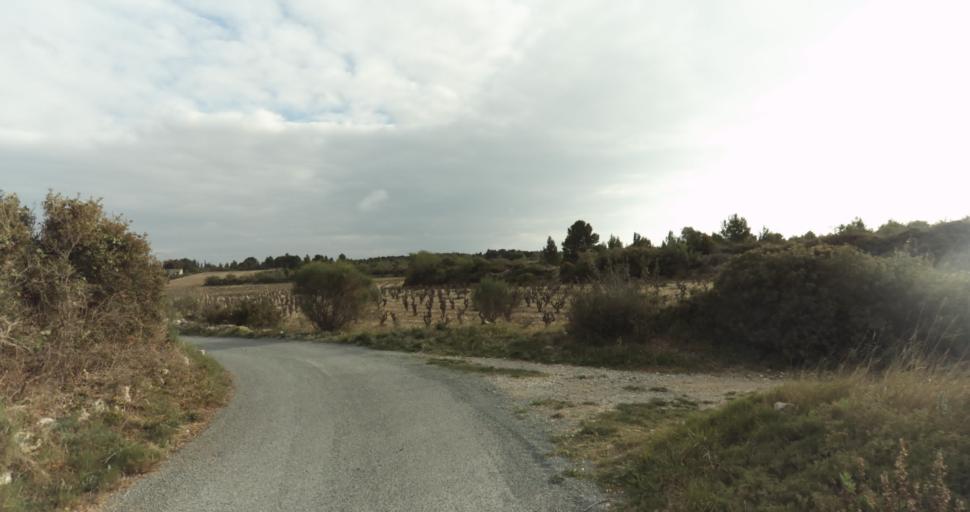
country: FR
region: Languedoc-Roussillon
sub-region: Departement de l'Aude
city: Leucate
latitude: 42.9248
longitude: 3.0282
